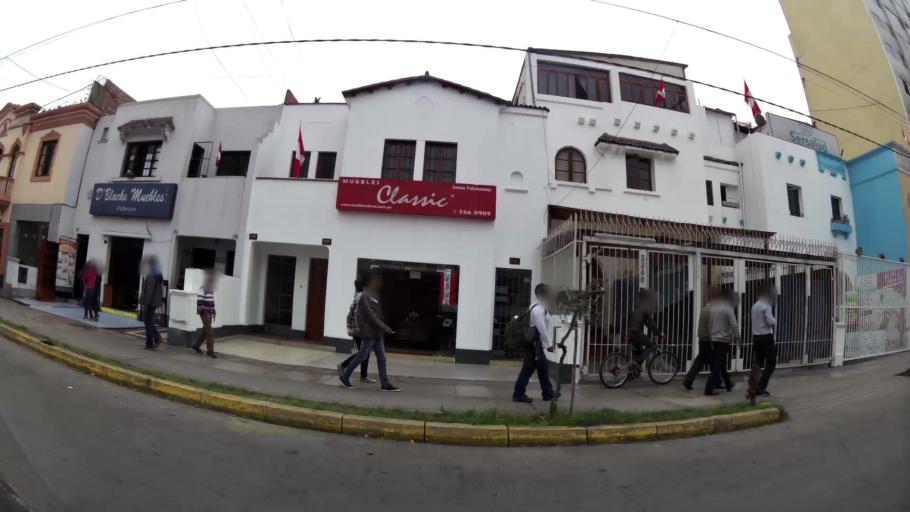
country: PE
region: Lima
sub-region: Lima
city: San Isidro
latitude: -12.0877
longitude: -77.0351
